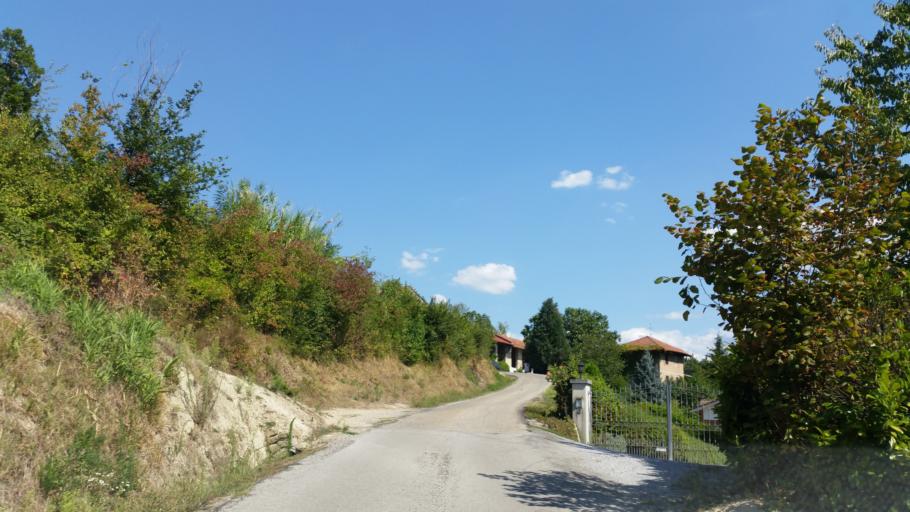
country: IT
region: Piedmont
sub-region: Provincia di Cuneo
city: Sinio
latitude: 44.5993
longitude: 8.0099
